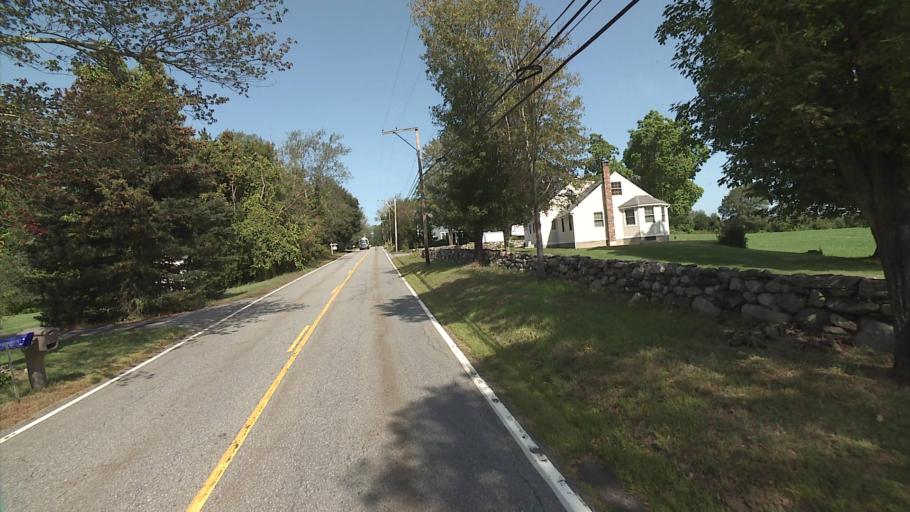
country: US
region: Connecticut
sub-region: Windham County
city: South Woodstock
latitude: 41.9680
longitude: -71.9876
